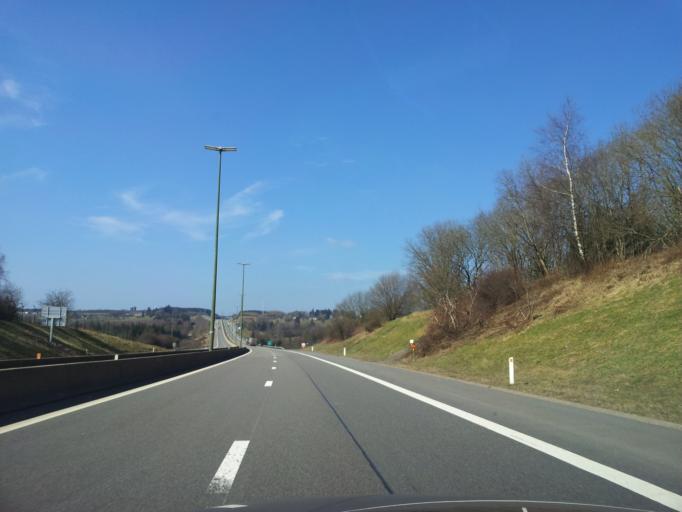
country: BE
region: Wallonia
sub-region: Province de Liege
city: Malmedy
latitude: 50.4711
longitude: 5.9842
